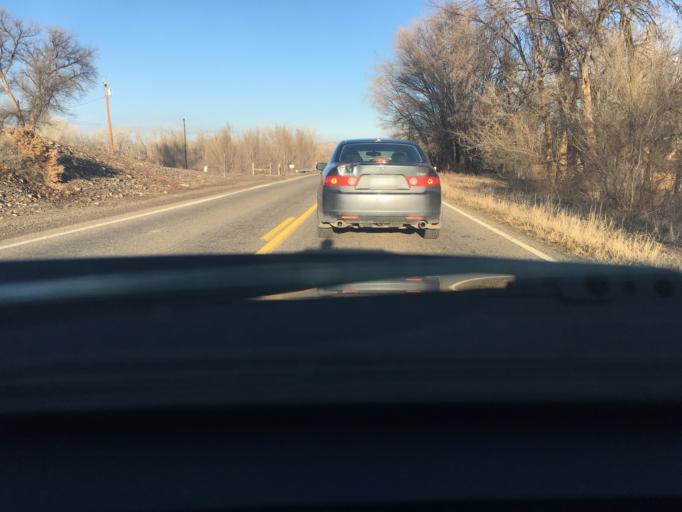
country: US
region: Colorado
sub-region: Delta County
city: Delta
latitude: 38.7462
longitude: -108.1173
